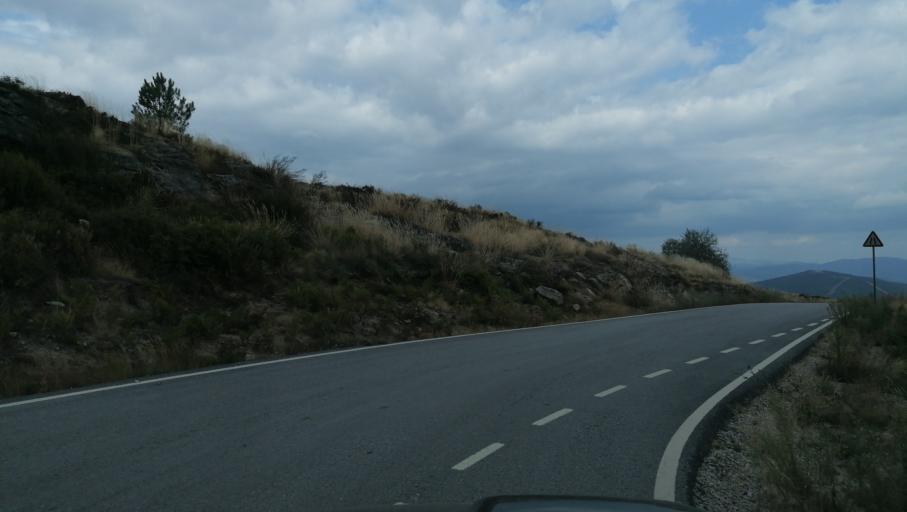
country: PT
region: Vila Real
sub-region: Vila Pouca de Aguiar
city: Vila Pouca de Aguiar
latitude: 41.5484
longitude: -7.6521
